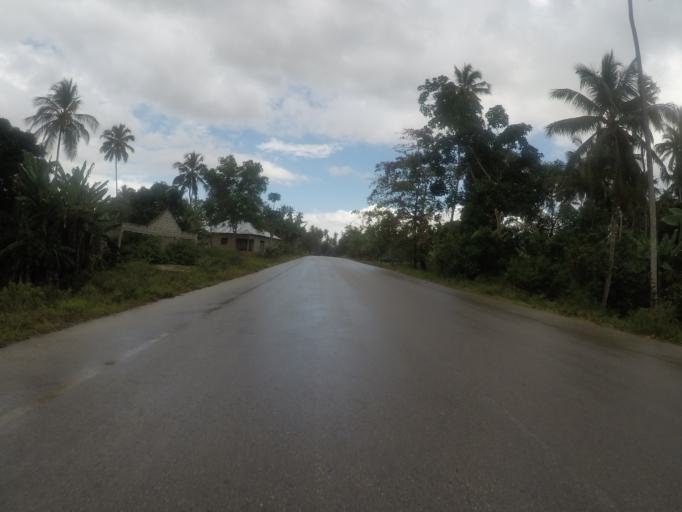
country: TZ
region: Zanzibar Central/South
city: Koani
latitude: -6.0308
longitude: 39.2176
